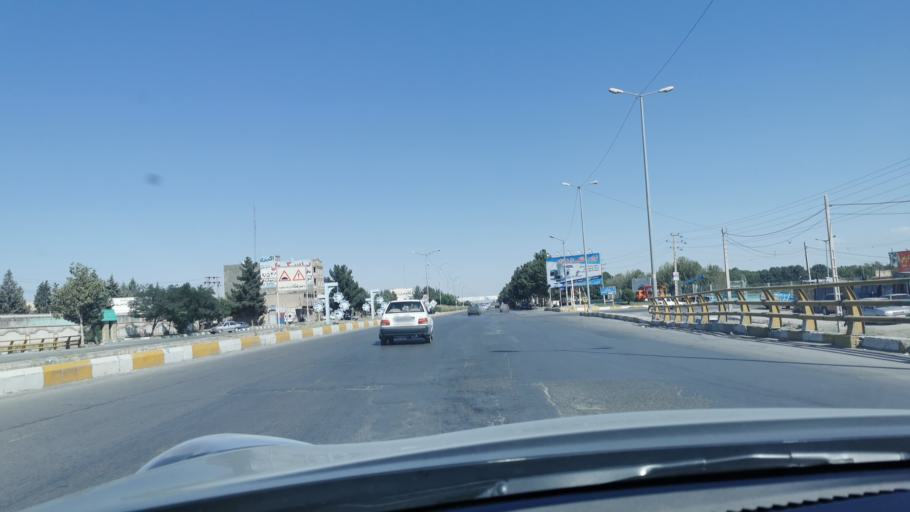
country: IR
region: Razavi Khorasan
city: Chenaran
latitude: 36.6350
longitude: 59.1288
